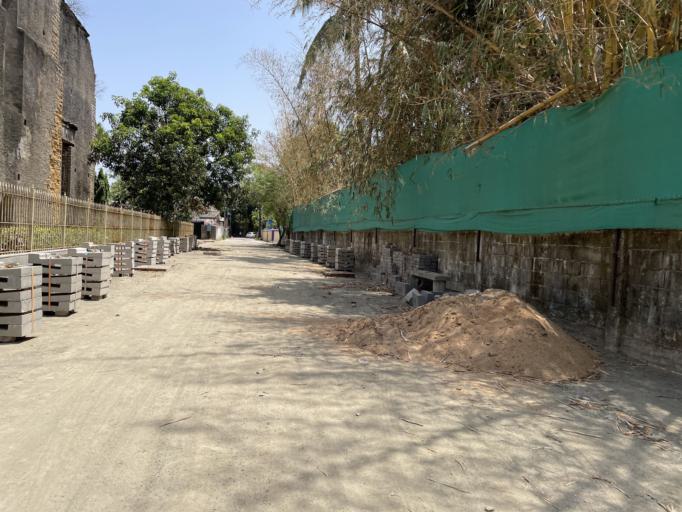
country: IN
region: Daman and Diu
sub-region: Daman District
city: Daman
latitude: 20.4074
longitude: 72.8312
